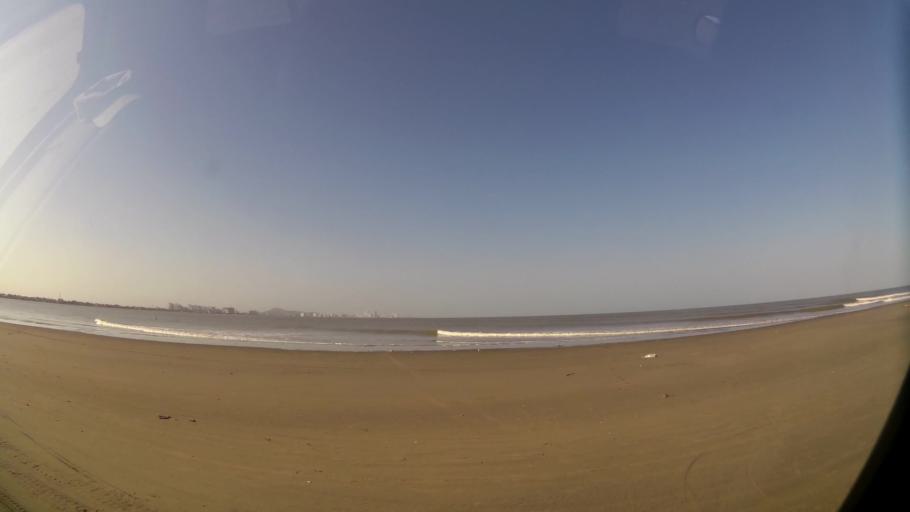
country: CO
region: Bolivar
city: Cartagena
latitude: 10.4931
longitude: -75.4957
